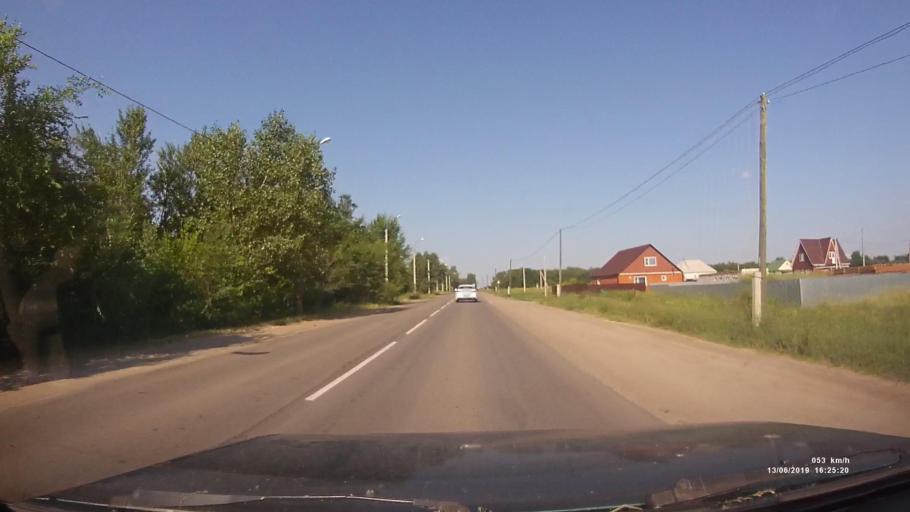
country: RU
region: Rostov
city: Kazanskaya
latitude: 49.7999
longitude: 41.1529
